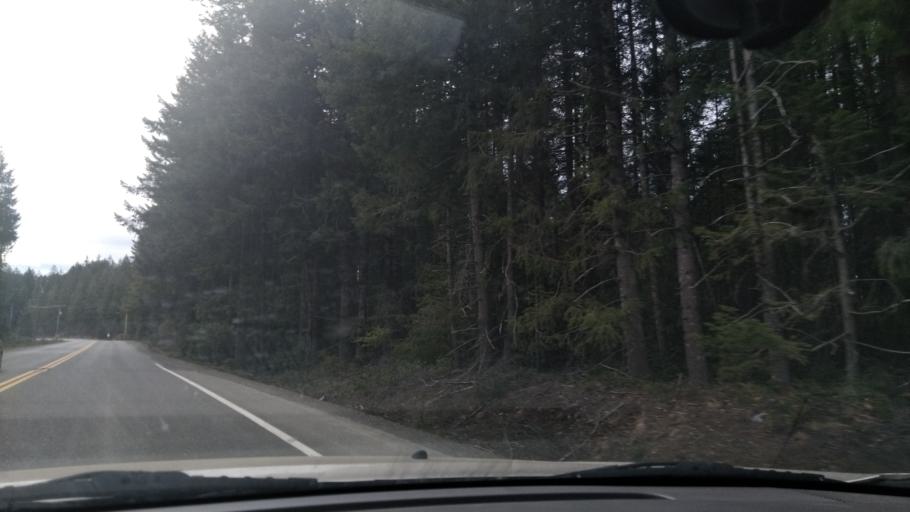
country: CA
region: British Columbia
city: Campbell River
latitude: 50.0043
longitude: -125.3665
